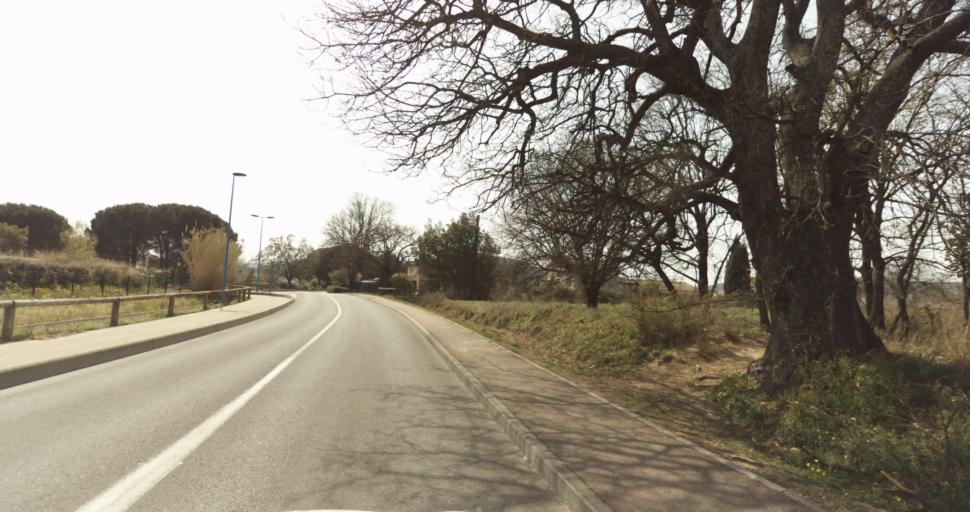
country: FR
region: Provence-Alpes-Cote d'Azur
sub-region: Departement du Var
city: Bormes-les-Mimosas
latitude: 43.1377
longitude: 6.3462
